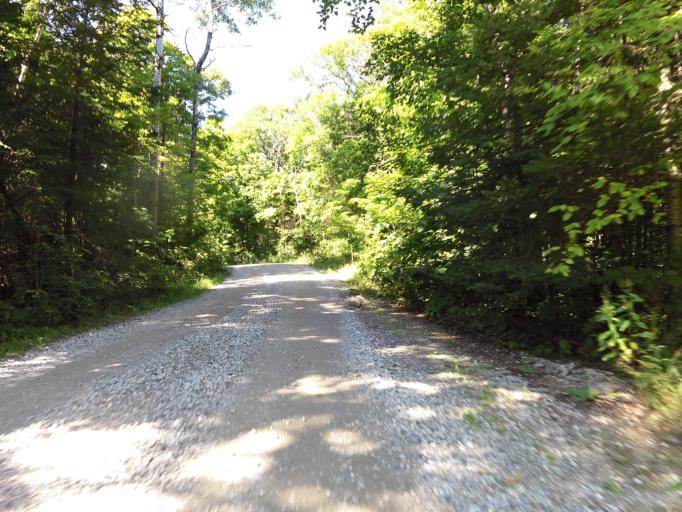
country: CA
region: Ontario
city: Renfrew
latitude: 45.1283
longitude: -76.7171
